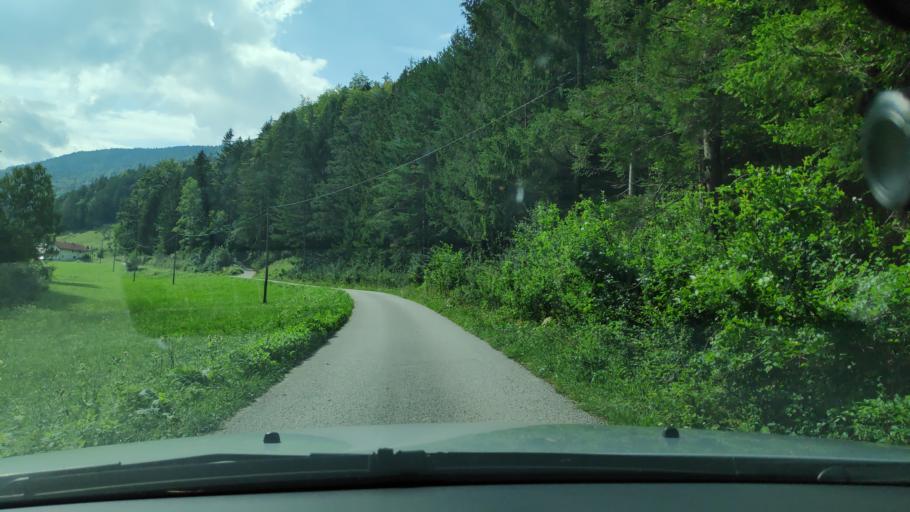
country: AT
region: Lower Austria
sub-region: Politischer Bezirk Wiener Neustadt
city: Miesenbach
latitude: 47.8367
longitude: 15.9596
